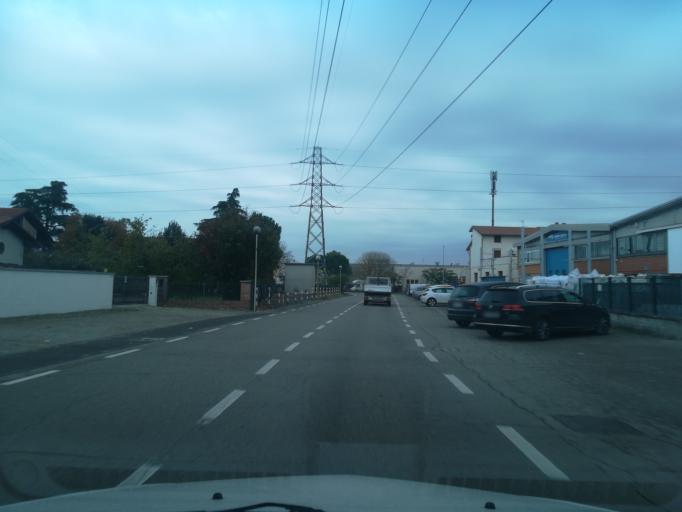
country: IT
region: Emilia-Romagna
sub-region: Provincia di Bologna
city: Imola
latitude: 44.3698
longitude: 11.7120
